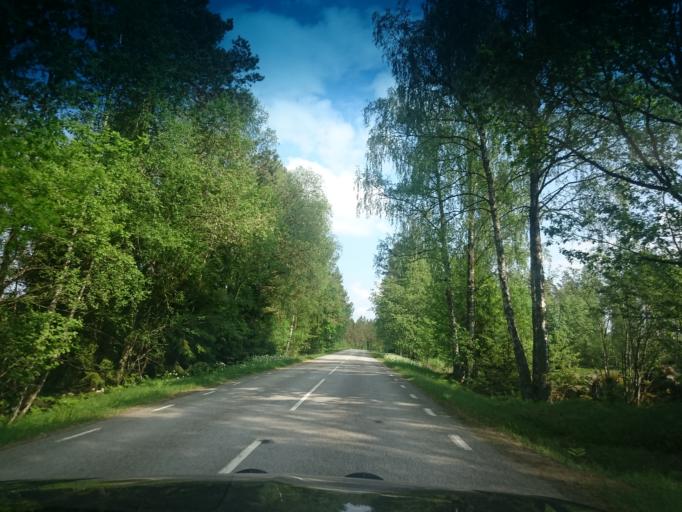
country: SE
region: Joenkoeping
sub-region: Vetlanda Kommun
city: Vetlanda
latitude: 57.3641
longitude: 15.0617
